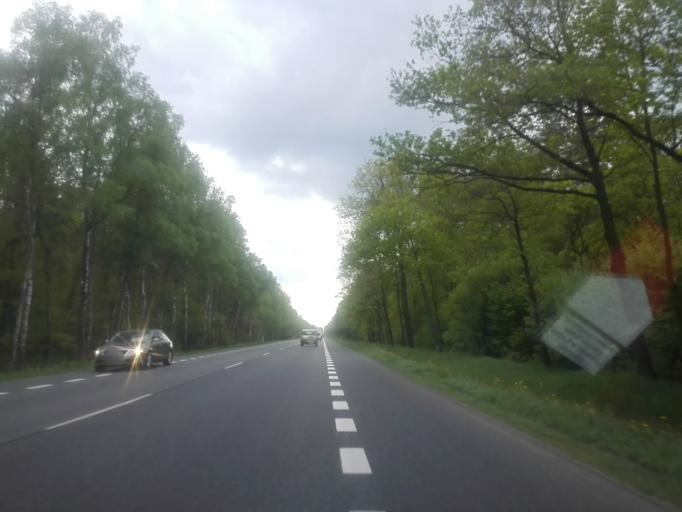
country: PL
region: Masovian Voivodeship
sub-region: Powiat ostrowski
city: Ostrow Mazowiecka
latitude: 52.8498
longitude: 21.9807
